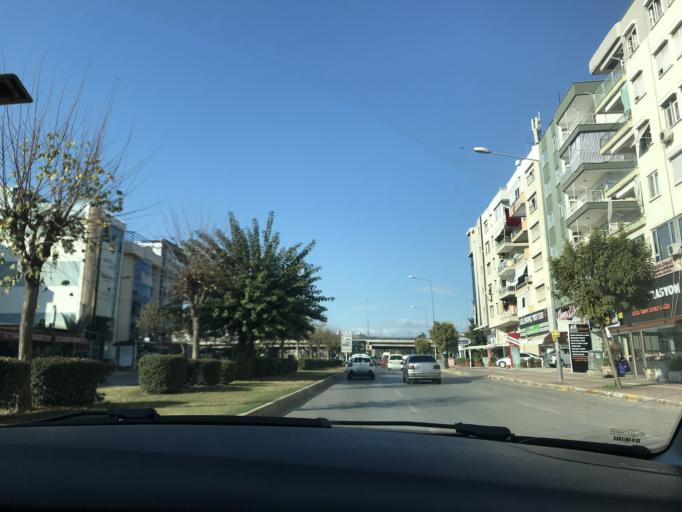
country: TR
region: Antalya
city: Antalya
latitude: 36.9093
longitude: 30.6987
